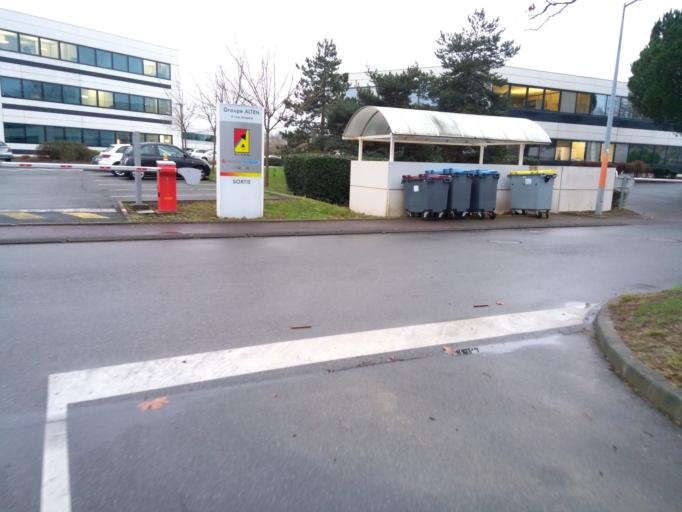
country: FR
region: Midi-Pyrenees
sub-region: Departement de la Haute-Garonne
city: Saint-Orens-de-Gameville
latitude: 43.5490
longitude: 1.5050
